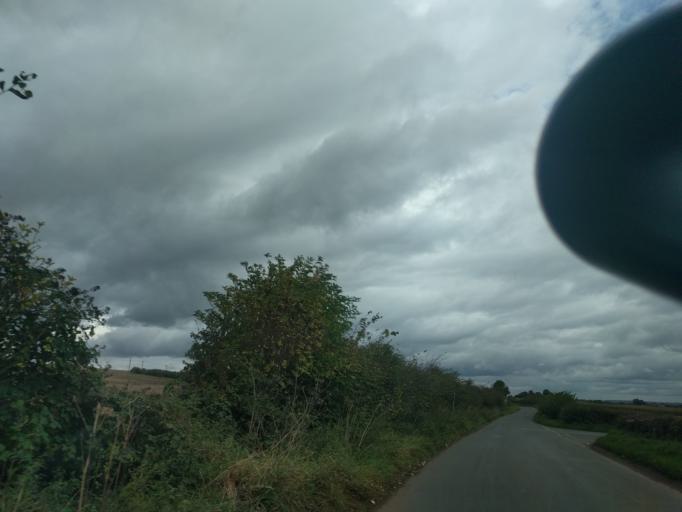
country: GB
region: England
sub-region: North Yorkshire
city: Bedale
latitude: 54.3344
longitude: -1.5747
